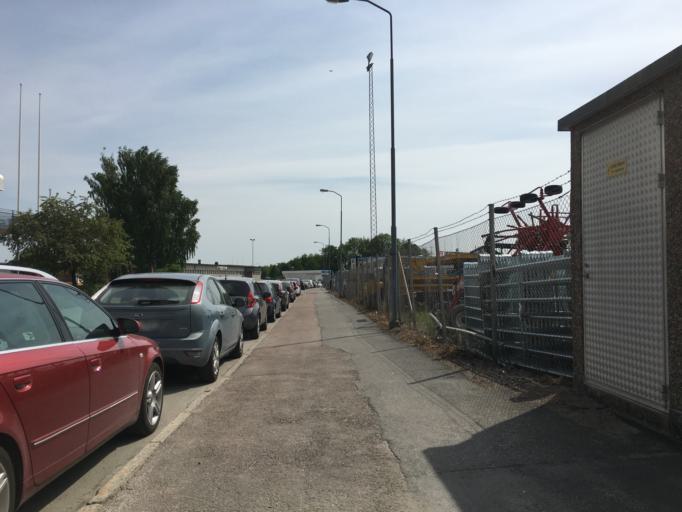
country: SE
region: Uppsala
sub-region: Uppsala Kommun
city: Uppsala
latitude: 59.8486
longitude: 17.6740
